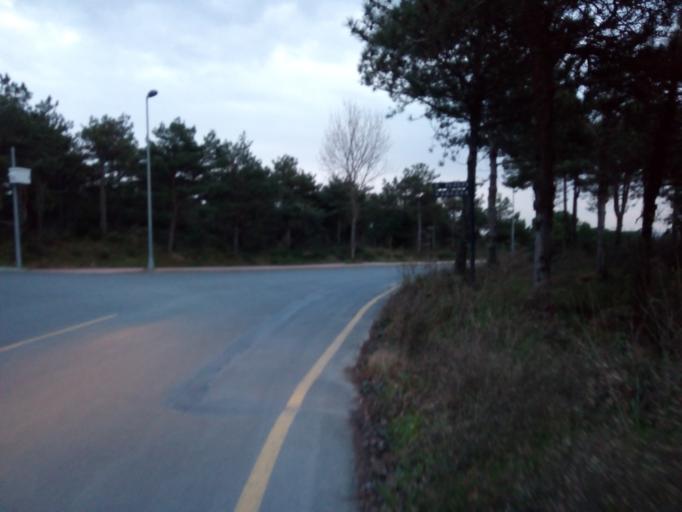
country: TR
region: Istanbul
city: Sisli
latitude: 41.1049
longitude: 29.0311
